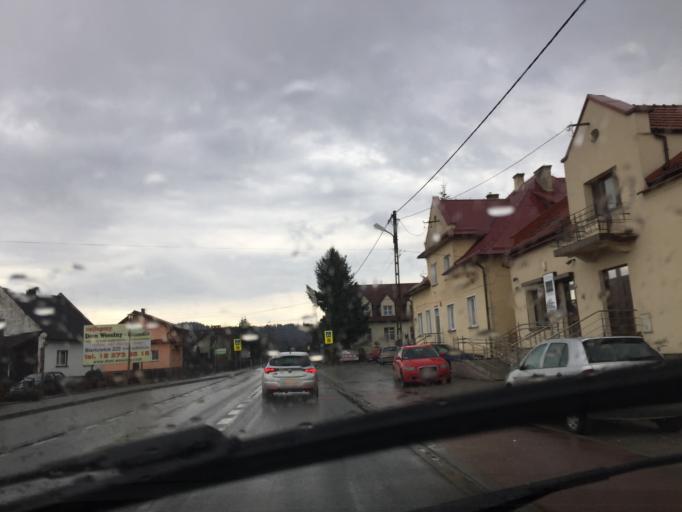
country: PL
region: Lesser Poland Voivodeship
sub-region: Powiat wadowicki
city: Izdebnik
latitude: 49.8720
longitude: 19.7921
